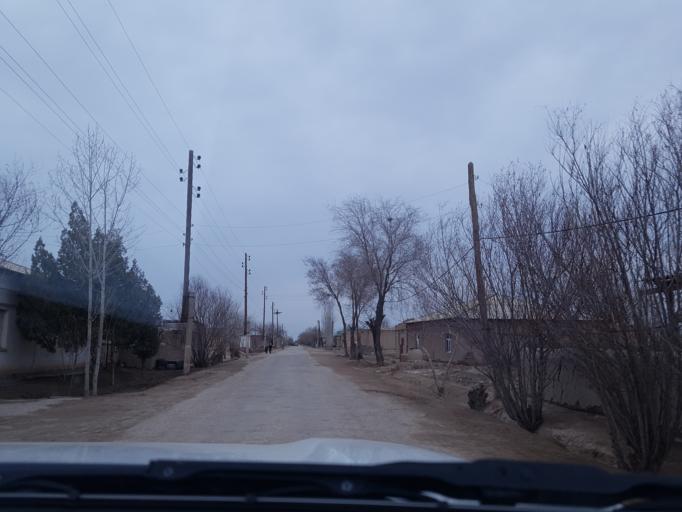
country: TM
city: Akdepe
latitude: 41.9834
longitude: 59.4719
